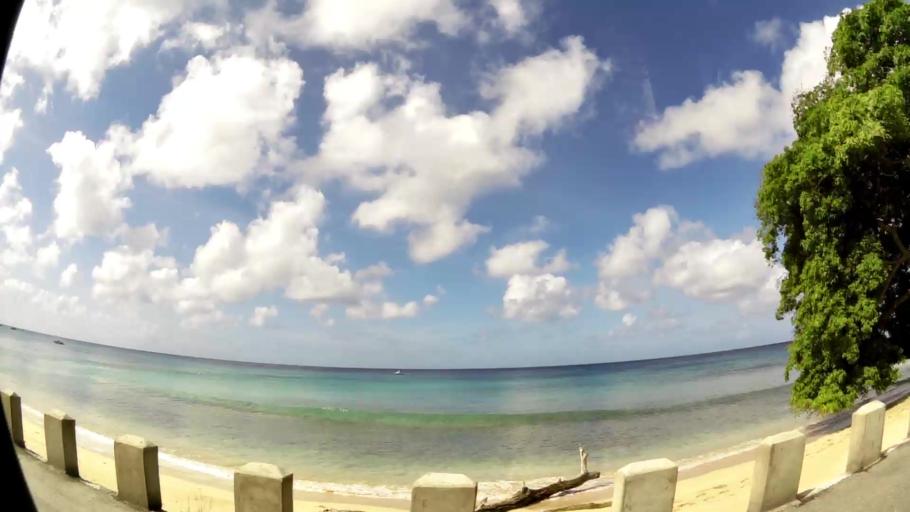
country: BB
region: Saint Lucy
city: Checker Hall
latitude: 13.2733
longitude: -59.6466
